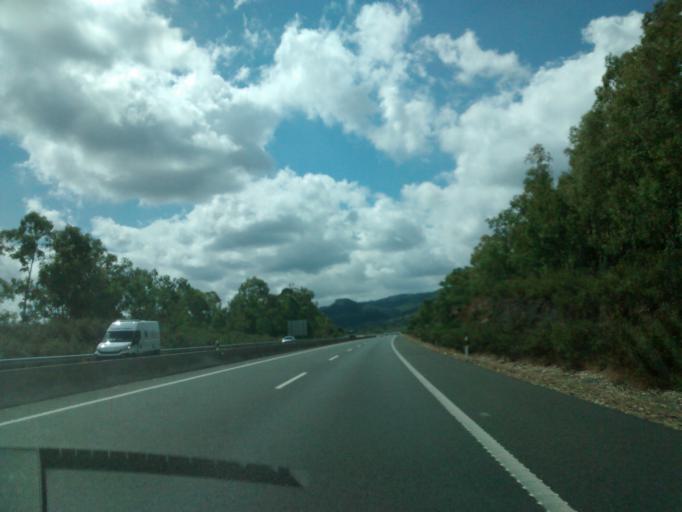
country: ES
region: Extremadura
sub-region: Provincia de Caceres
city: Romangordo
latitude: 39.7221
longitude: -5.7120
